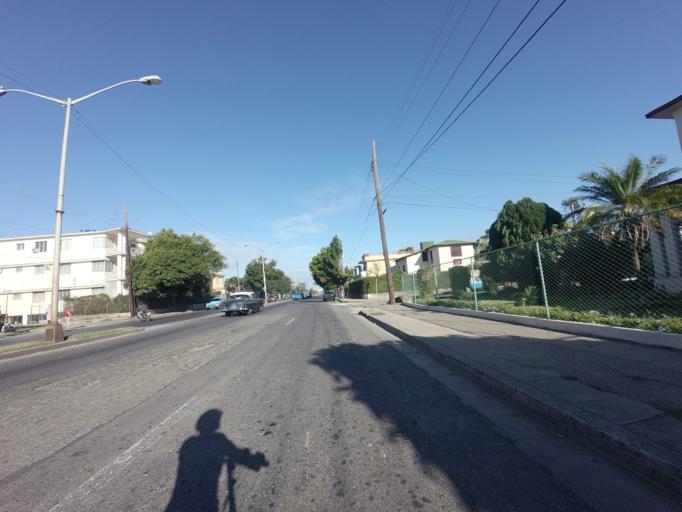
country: CU
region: La Habana
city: Cerro
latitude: 23.1005
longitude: -82.4379
